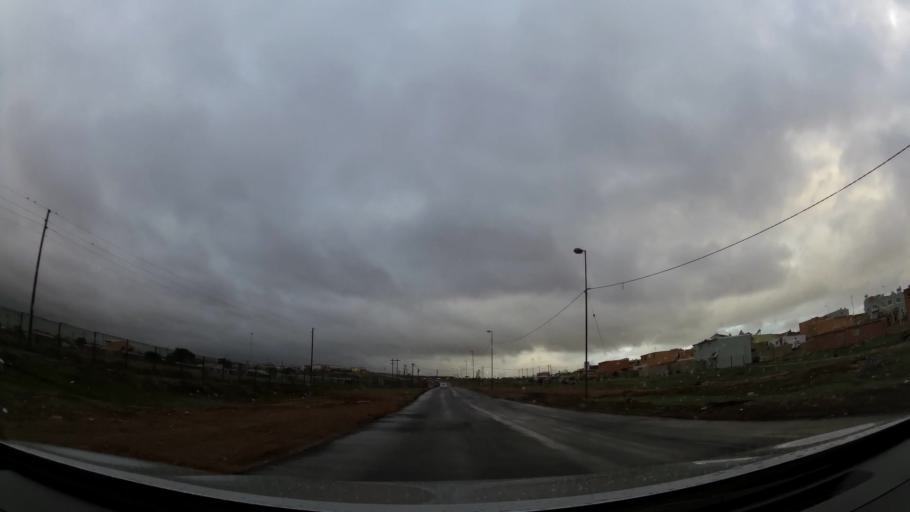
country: ZA
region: Eastern Cape
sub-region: Nelson Mandela Bay Metropolitan Municipality
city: Port Elizabeth
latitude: -33.8888
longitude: 25.5569
